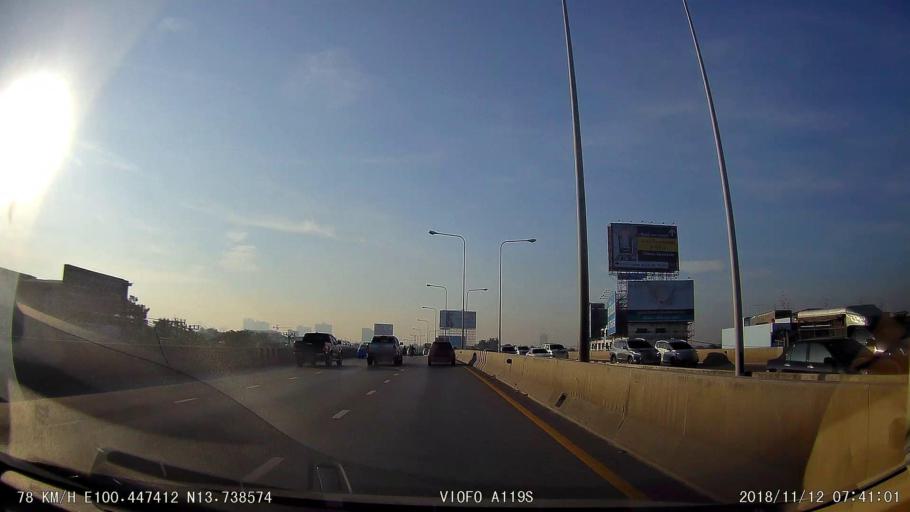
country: TH
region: Bangkok
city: Phasi Charoen
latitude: 13.7379
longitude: 100.4475
